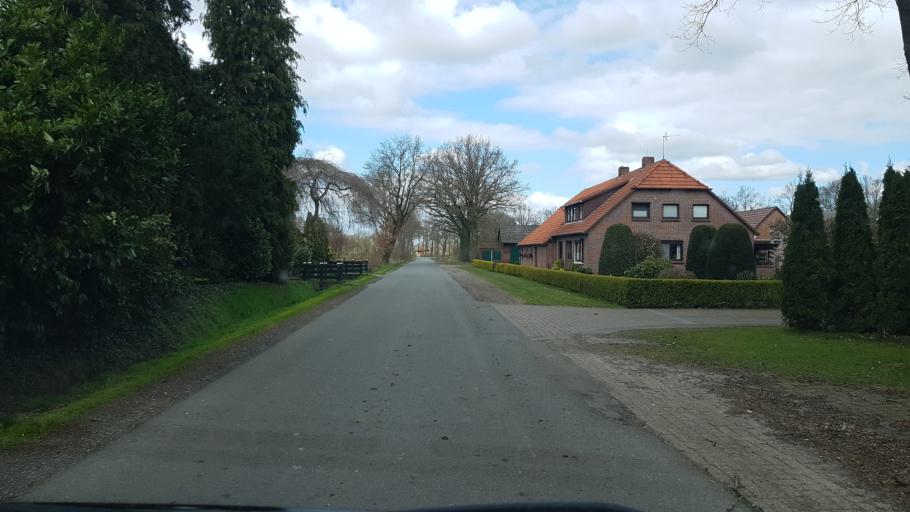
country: DE
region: Lower Saxony
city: Edewecht
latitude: 53.1001
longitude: 7.9462
